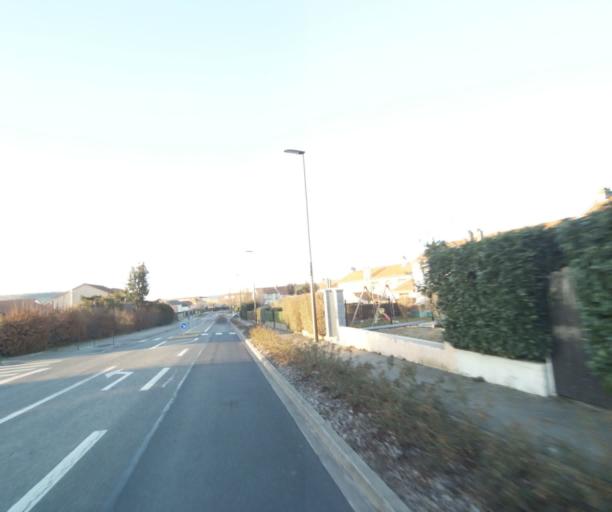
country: FR
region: Lorraine
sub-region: Departement de Meurthe-et-Moselle
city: Pulnoy
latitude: 48.6963
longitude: 6.2552
